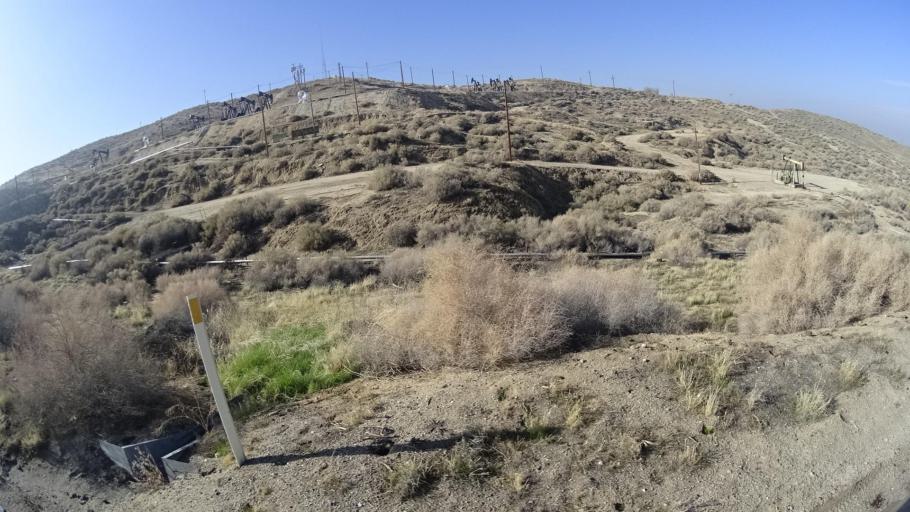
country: US
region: California
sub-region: Kern County
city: South Taft
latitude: 35.1188
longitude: -119.4563
